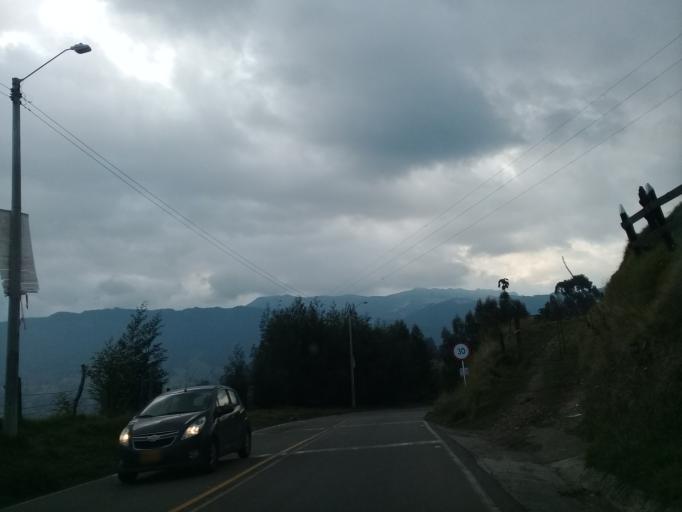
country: CO
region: Cundinamarca
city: Zipaquira
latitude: 5.0355
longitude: -74.0430
